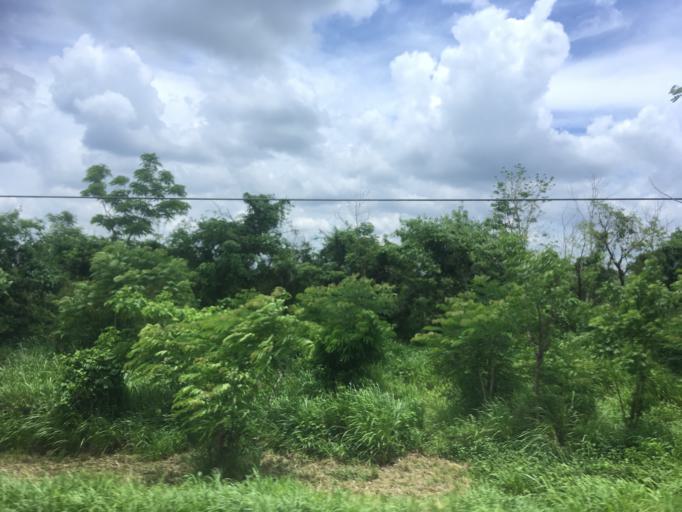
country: CU
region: Villa Clara
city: Esperanza
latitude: 22.4331
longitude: -80.0636
